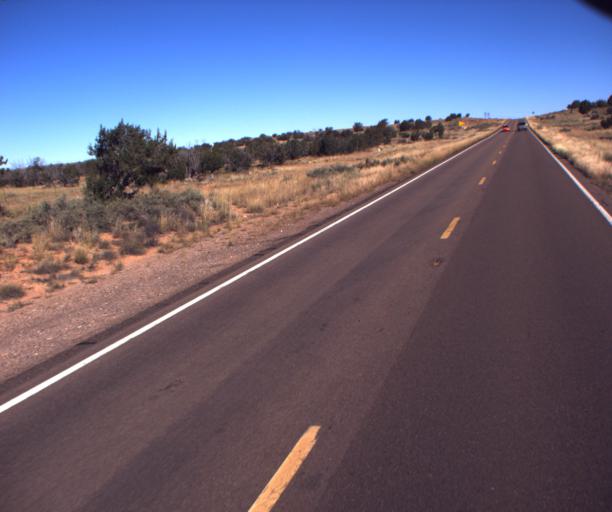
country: US
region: Arizona
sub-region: Navajo County
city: Snowflake
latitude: 34.6175
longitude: -110.0915
